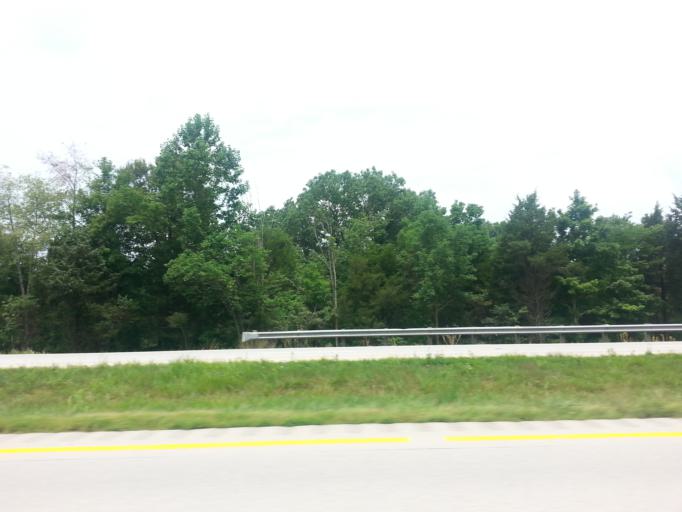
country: US
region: Kentucky
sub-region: Grayson County
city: Leitchfield
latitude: 37.5615
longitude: -86.0661
